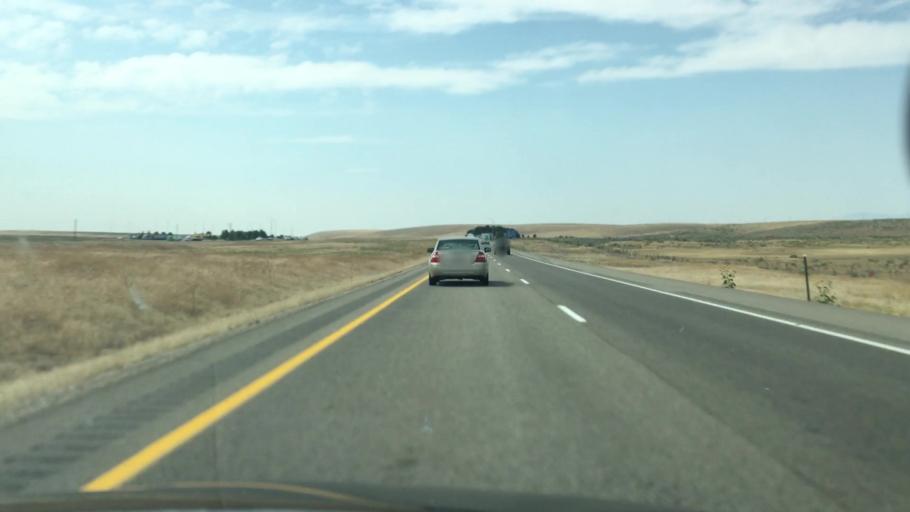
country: US
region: Idaho
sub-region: Ada County
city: Boise
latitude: 43.4722
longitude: -116.0999
